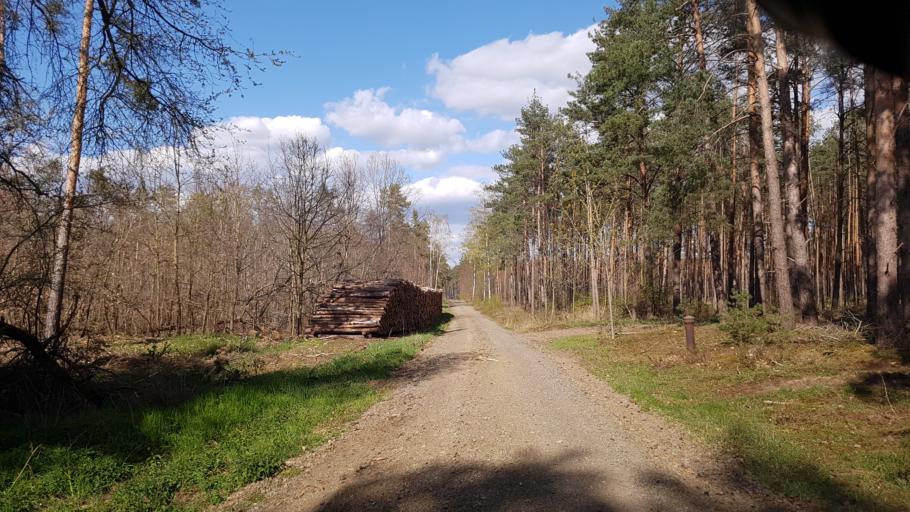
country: DE
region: Brandenburg
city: Muhlberg
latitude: 51.4801
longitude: 13.2805
